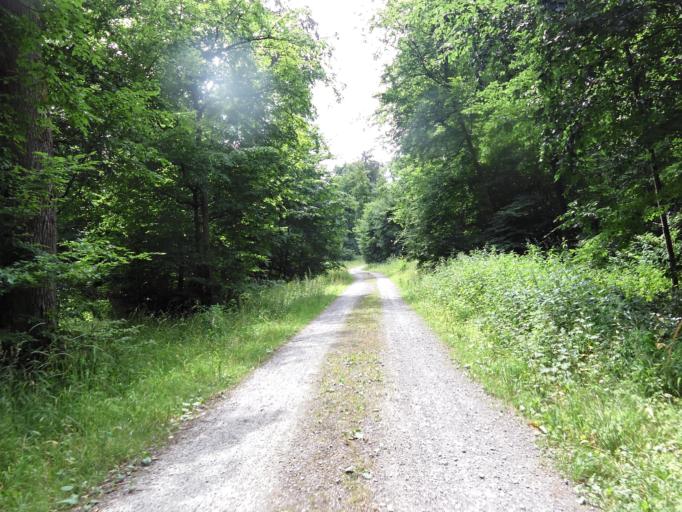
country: DE
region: Bavaria
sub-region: Regierungsbezirk Unterfranken
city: Wuerzburg
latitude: 49.7496
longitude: 9.8835
